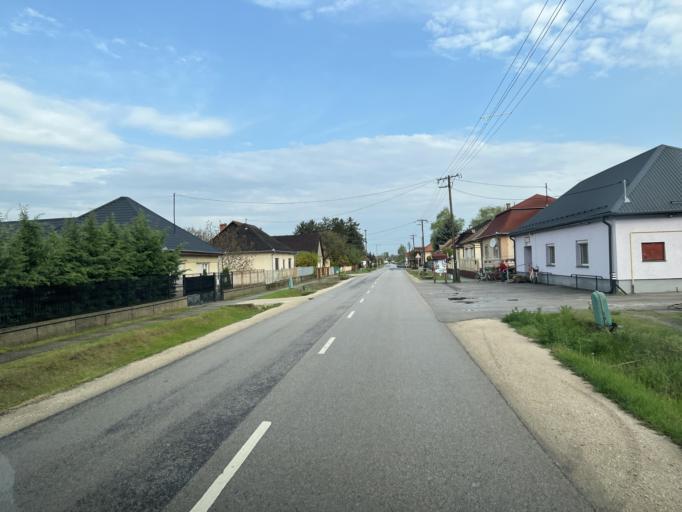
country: HU
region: Pest
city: Nyaregyhaza
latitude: 47.2267
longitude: 19.4540
